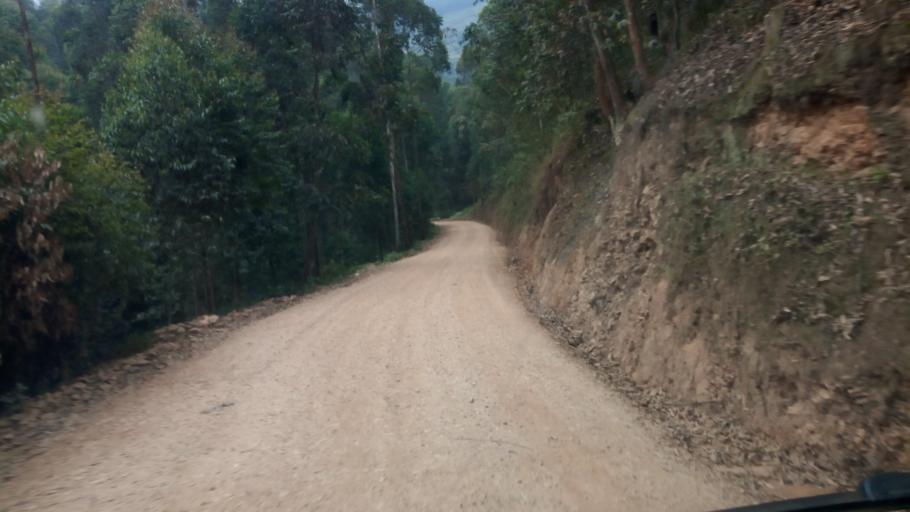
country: UG
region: Western Region
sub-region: Kanungu District
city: Kanungu
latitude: -1.0963
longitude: 29.8462
